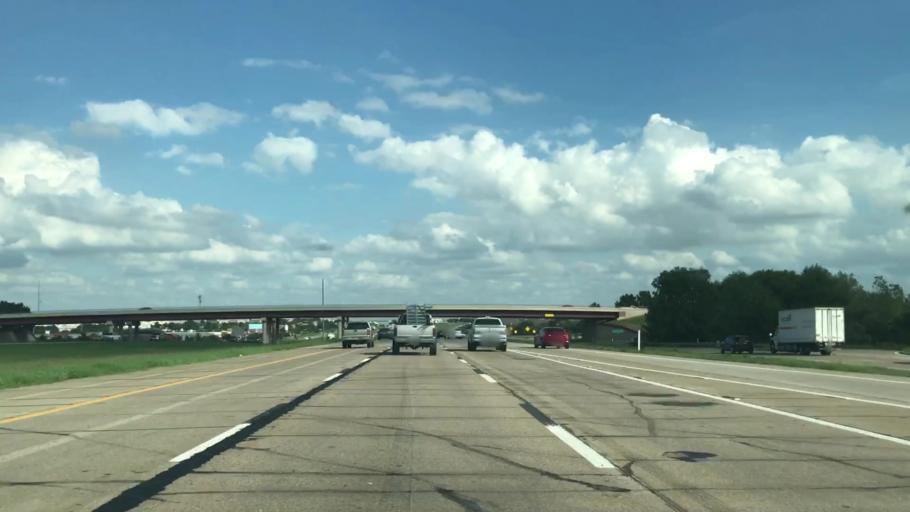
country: US
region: Texas
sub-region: Dallas County
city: Coppell
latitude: 32.9194
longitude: -96.9774
